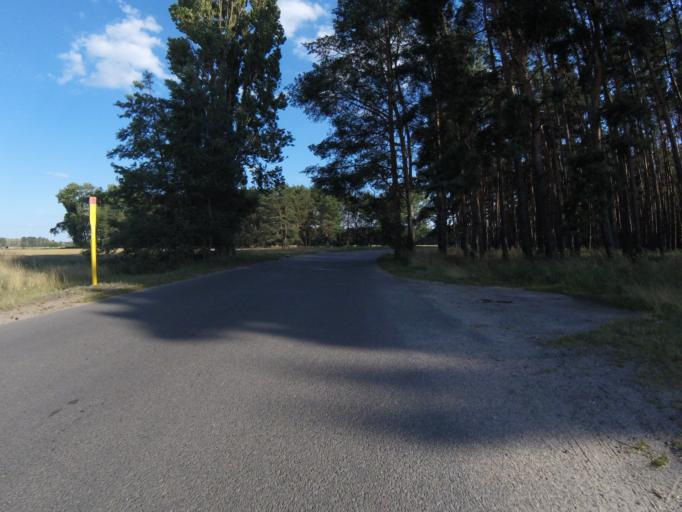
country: DE
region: Brandenburg
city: Mittenwalde
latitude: 52.2338
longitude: 13.5127
